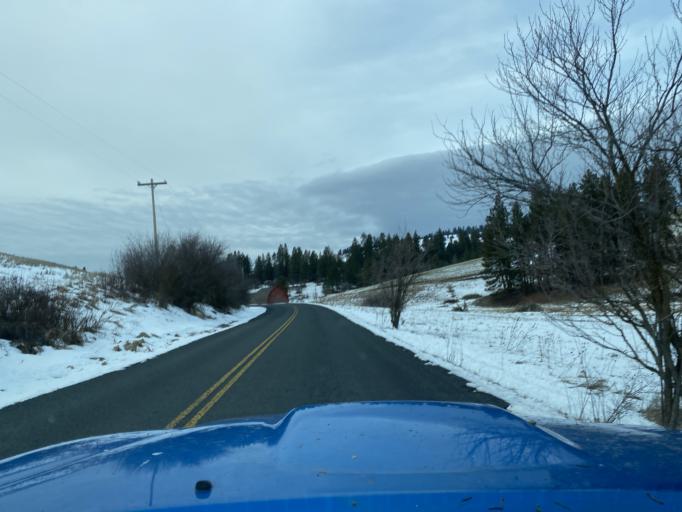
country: US
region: Idaho
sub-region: Latah County
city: Moscow
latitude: 46.6921
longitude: -116.9129
